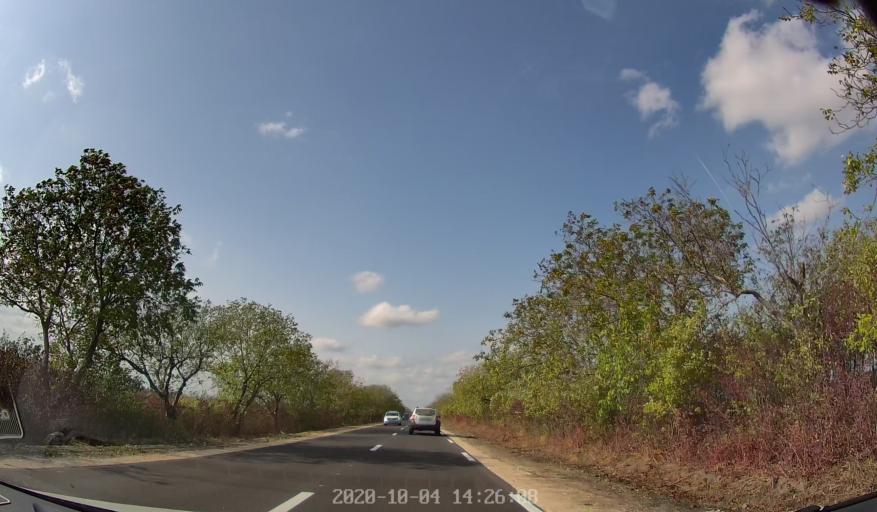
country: MD
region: Rezina
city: Saharna
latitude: 47.6248
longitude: 28.8892
